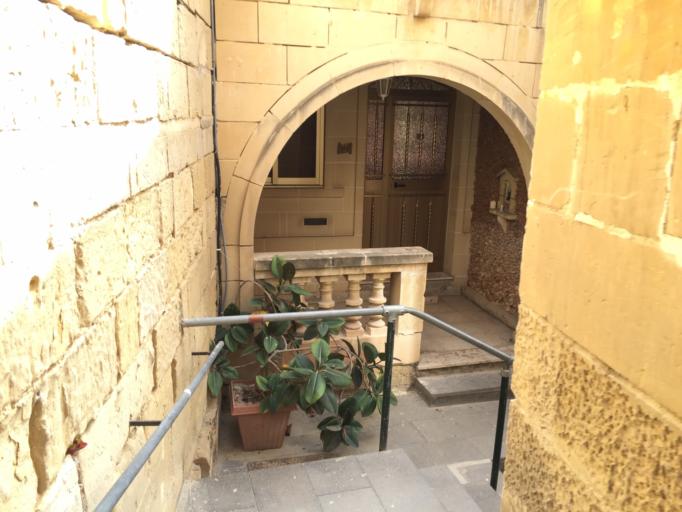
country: MT
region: Bormla
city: Cospicua
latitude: 35.8898
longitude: 14.5267
